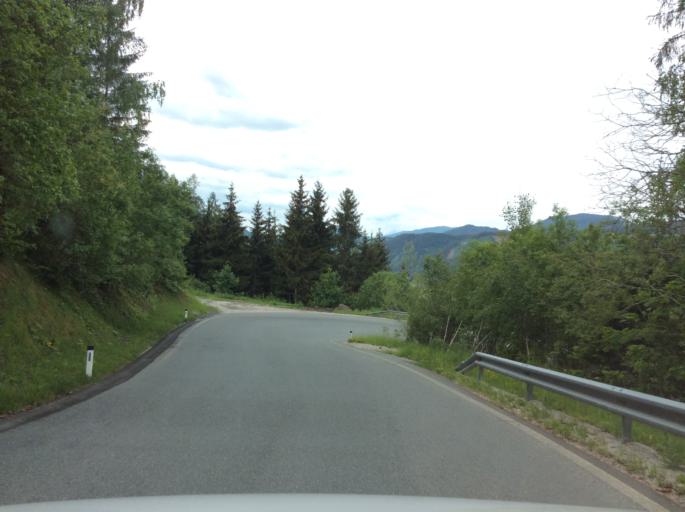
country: AT
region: Styria
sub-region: Politischer Bezirk Liezen
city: Schladming
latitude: 47.3935
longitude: 13.7099
